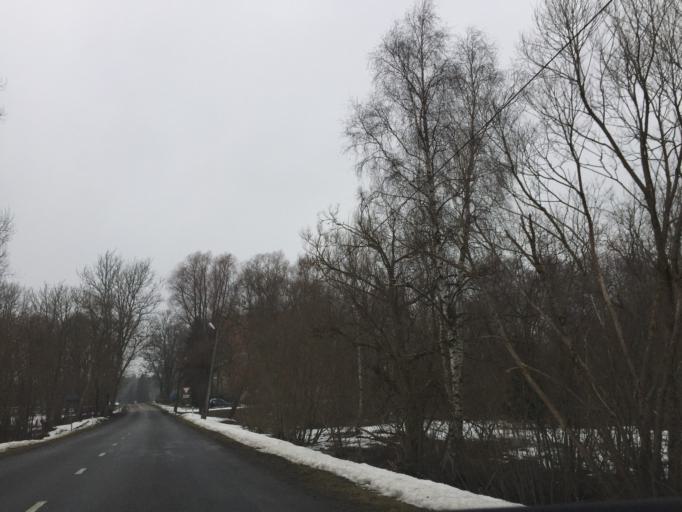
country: EE
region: Saare
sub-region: Kuressaare linn
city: Kuressaare
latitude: 58.4069
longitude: 22.7909
